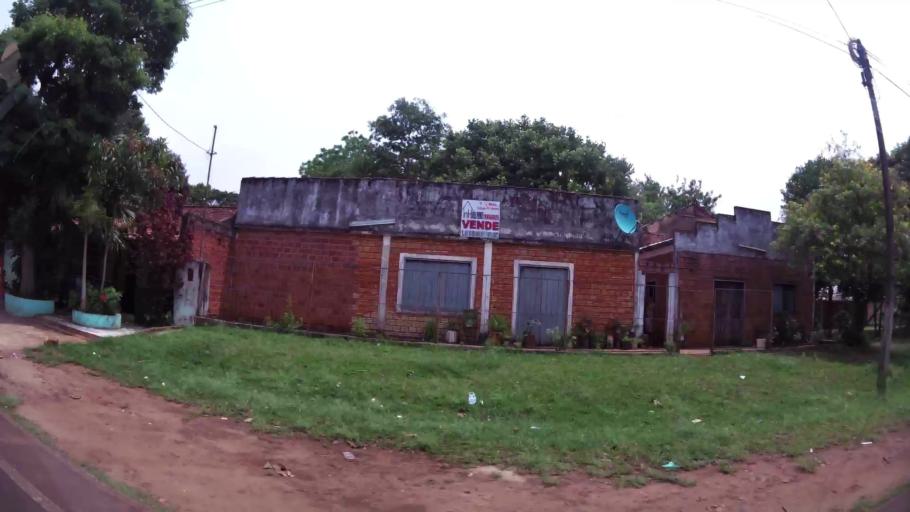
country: AR
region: Misiones
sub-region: Departamento de Iguazu
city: Puerto Iguazu
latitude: -25.5954
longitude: -54.6022
